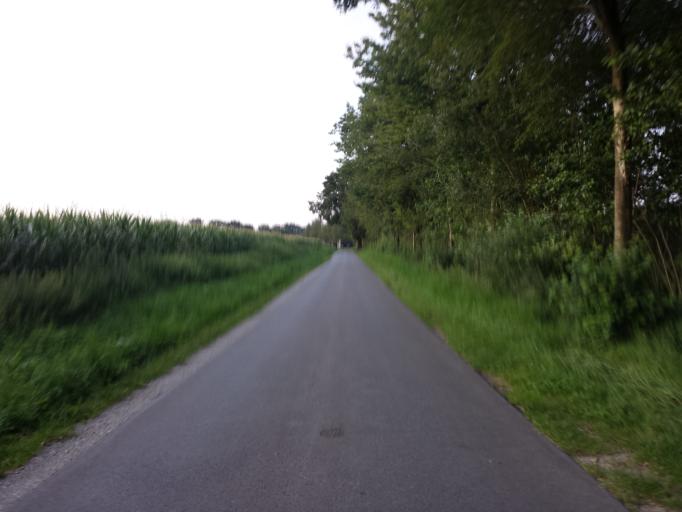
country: DE
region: North Rhine-Westphalia
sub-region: Regierungsbezirk Detmold
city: Harsewinkel
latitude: 51.9710
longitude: 8.2501
